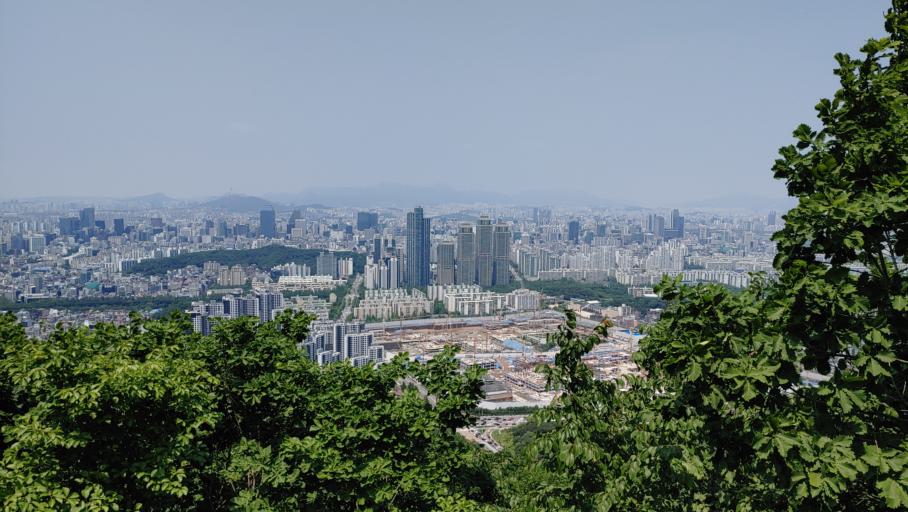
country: KR
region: Gyeonggi-do
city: Seongnam-si
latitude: 37.4690
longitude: 127.0616
